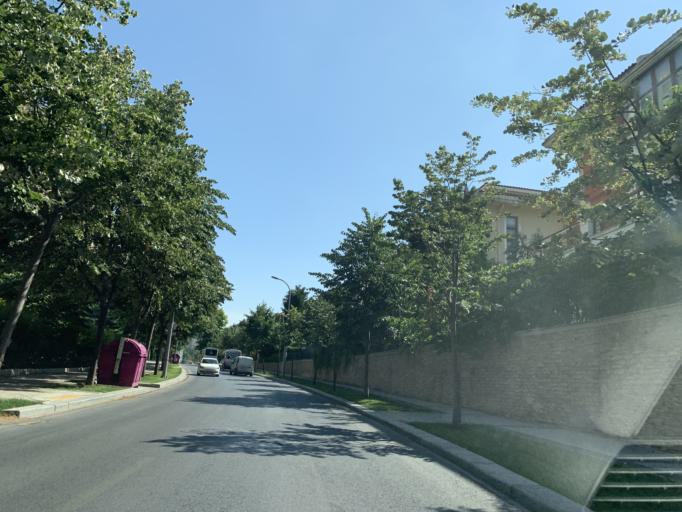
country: TR
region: Istanbul
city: Esenyurt
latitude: 41.0718
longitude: 28.6786
